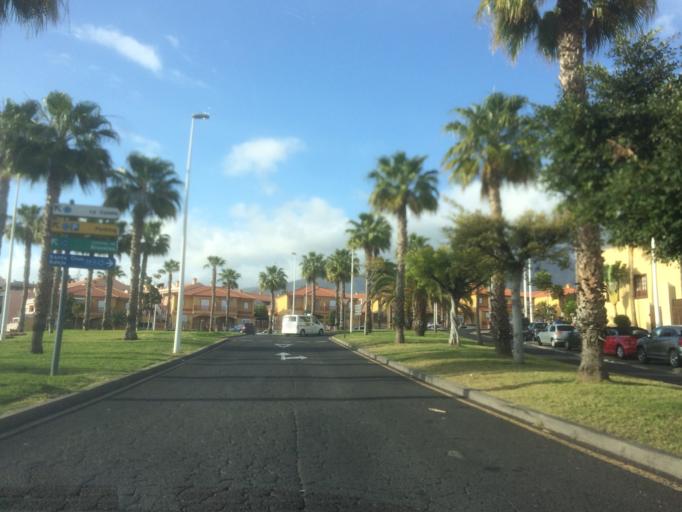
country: ES
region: Canary Islands
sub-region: Provincia de Santa Cruz de Tenerife
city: Playa de las Americas
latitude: 28.0907
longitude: -16.7348
